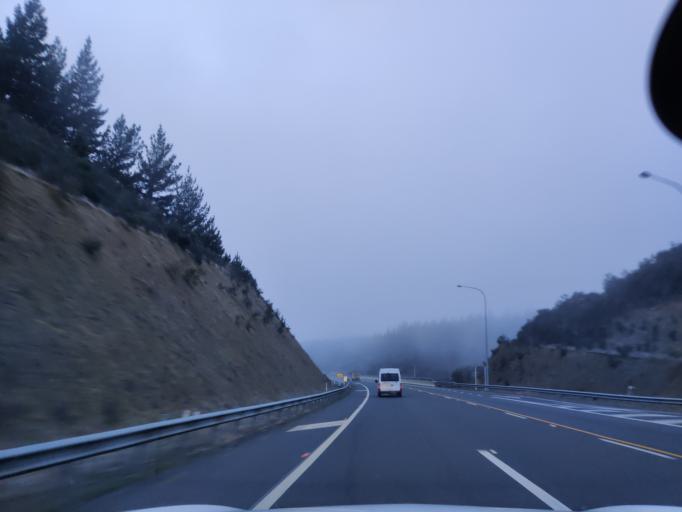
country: NZ
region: Waikato
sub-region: South Waikato District
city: Tokoroa
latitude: -38.3915
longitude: 176.0123
